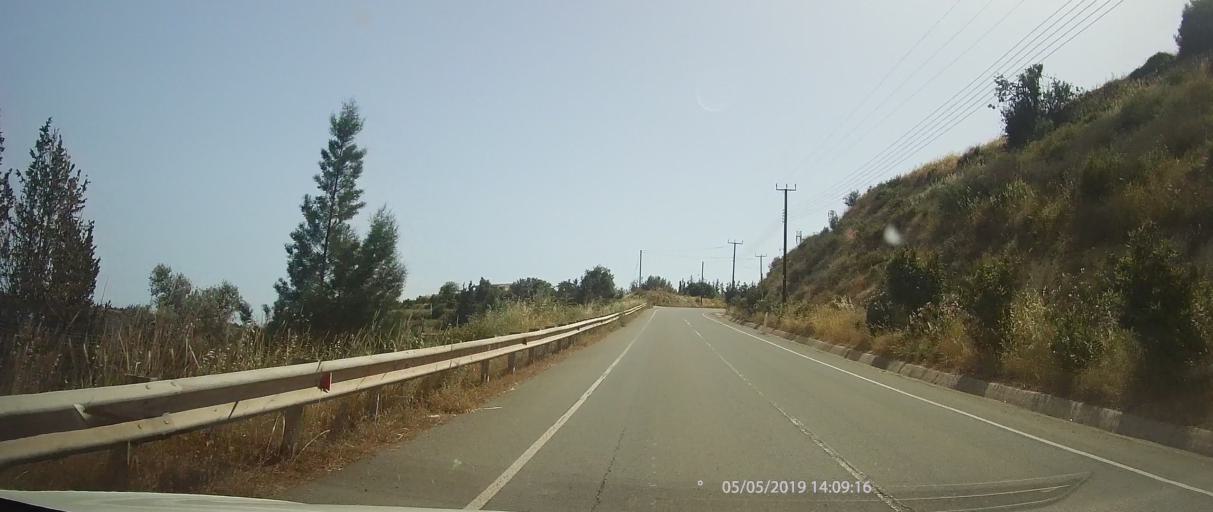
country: CY
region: Limassol
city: Pissouri
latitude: 34.7294
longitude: 32.5735
